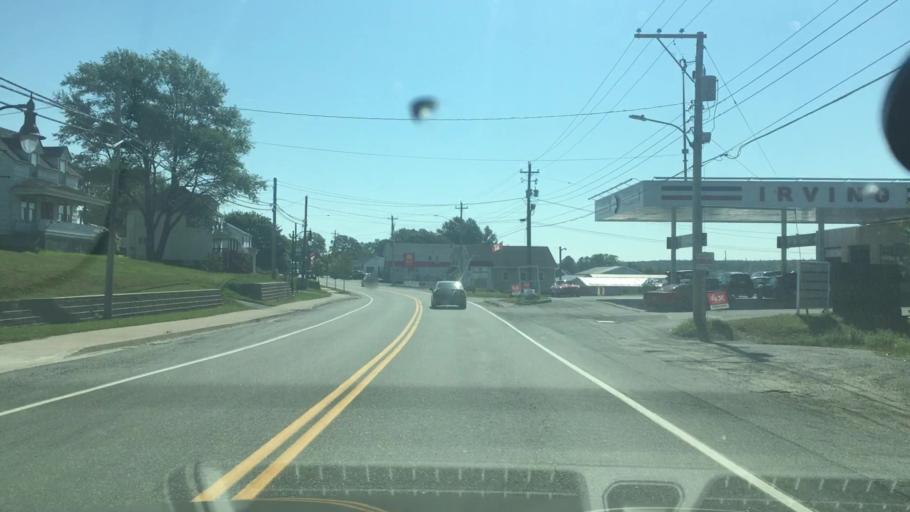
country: CA
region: Nova Scotia
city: New Glasgow
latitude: 44.9247
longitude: -62.5400
